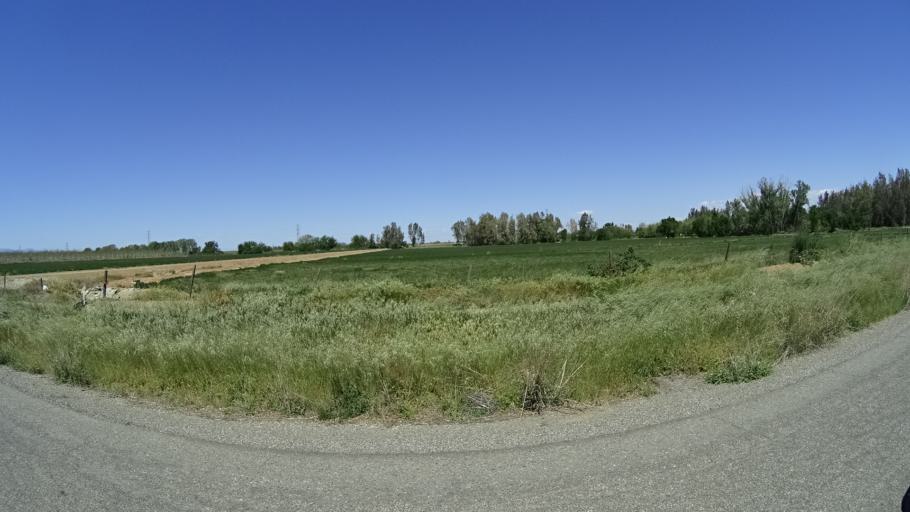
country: US
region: California
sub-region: Glenn County
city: Orland
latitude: 39.7942
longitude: -122.1876
